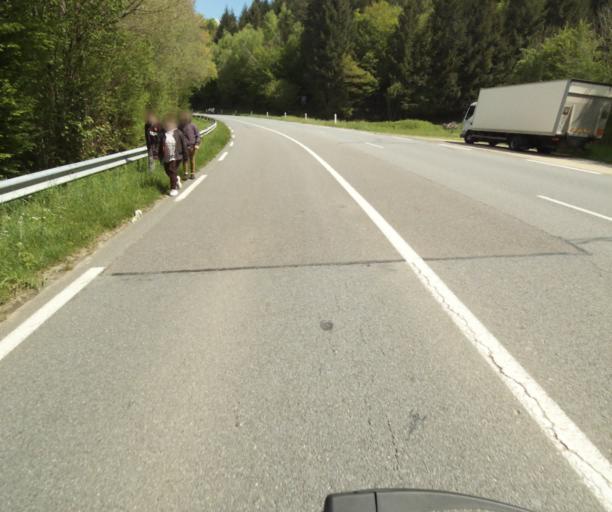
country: FR
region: Limousin
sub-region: Departement de la Correze
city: Naves
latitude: 45.2907
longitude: 1.7742
